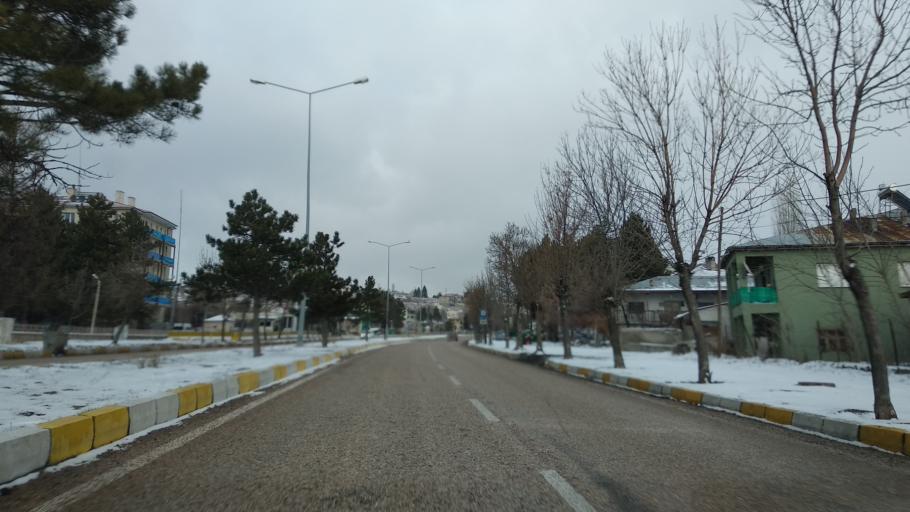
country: TR
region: Kayseri
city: Pinarbasi
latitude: 38.7203
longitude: 36.3860
